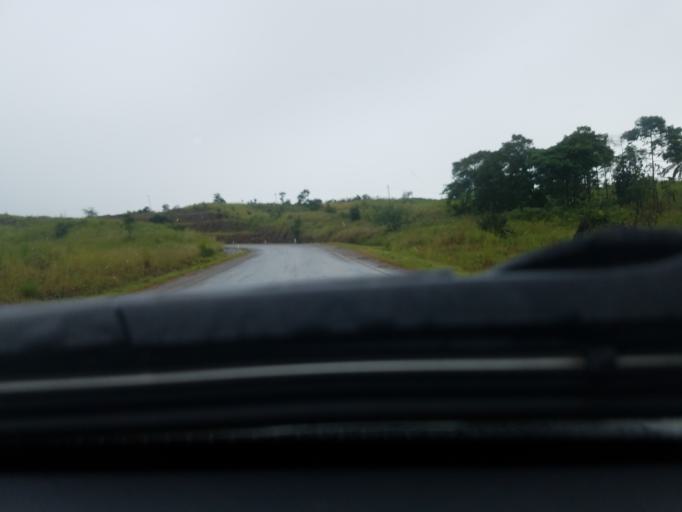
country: TZ
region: Kigoma
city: Mwandiga
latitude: -4.6684
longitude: 29.7248
